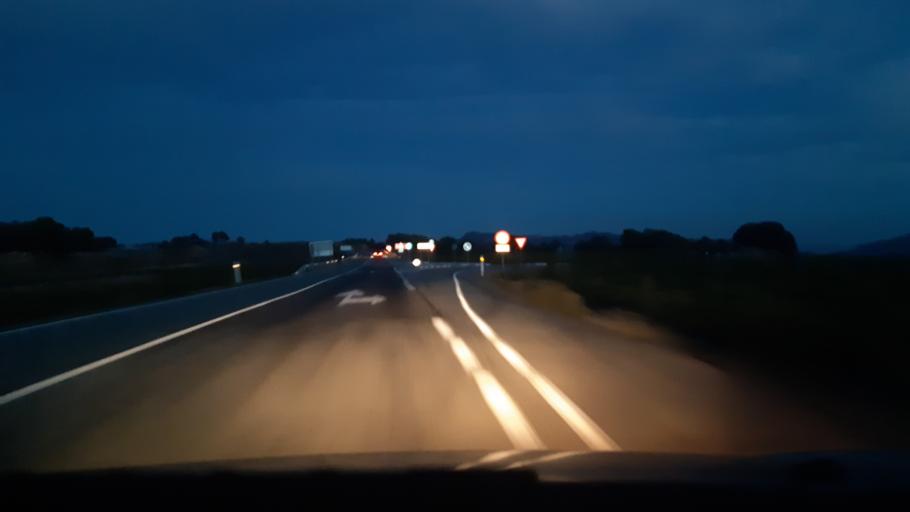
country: ES
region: Catalonia
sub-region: Provincia de Tarragona
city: Bot
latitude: 41.0493
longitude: 0.3695
